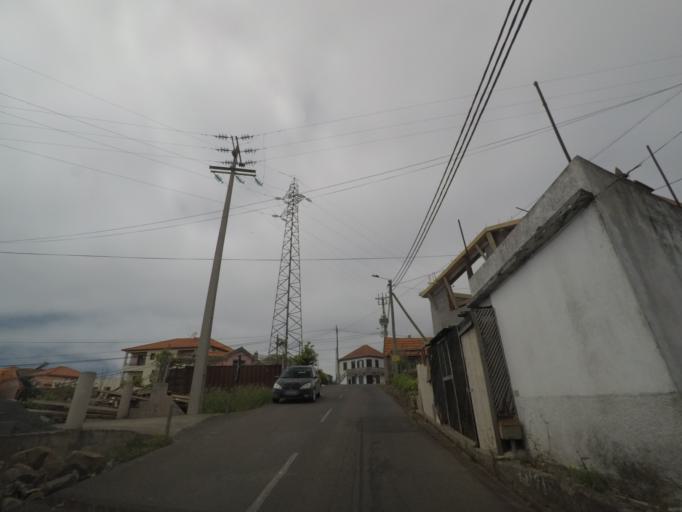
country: PT
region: Madeira
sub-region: Calheta
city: Arco da Calheta
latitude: 32.7088
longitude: -17.1163
